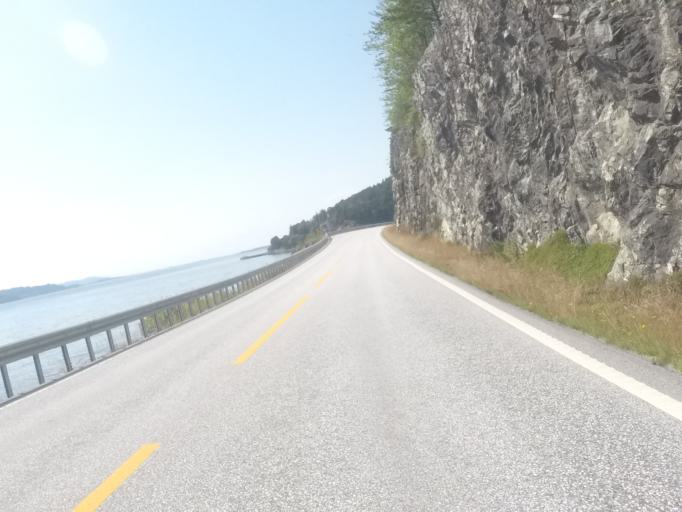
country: NO
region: Sogn og Fjordane
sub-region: Flora
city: Floro
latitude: 61.6035
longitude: 5.1673
